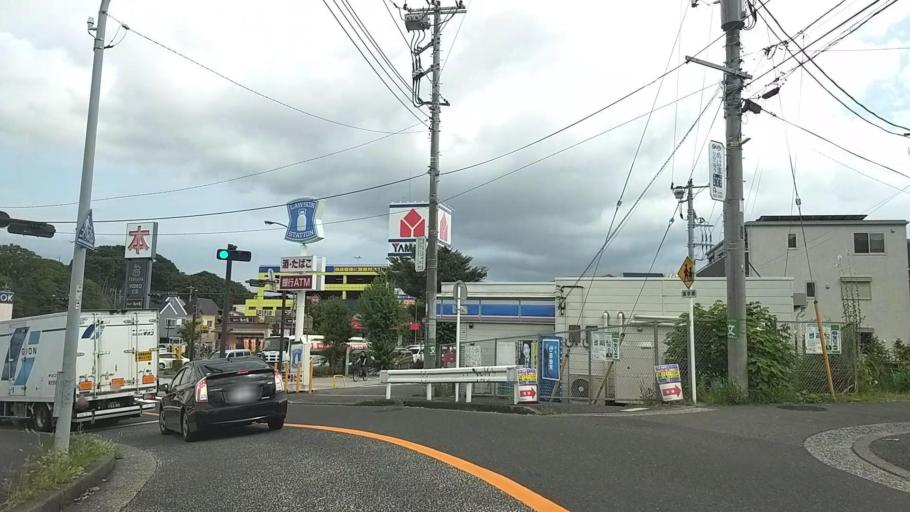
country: JP
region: Kanagawa
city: Yokohama
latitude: 35.4135
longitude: 139.5591
